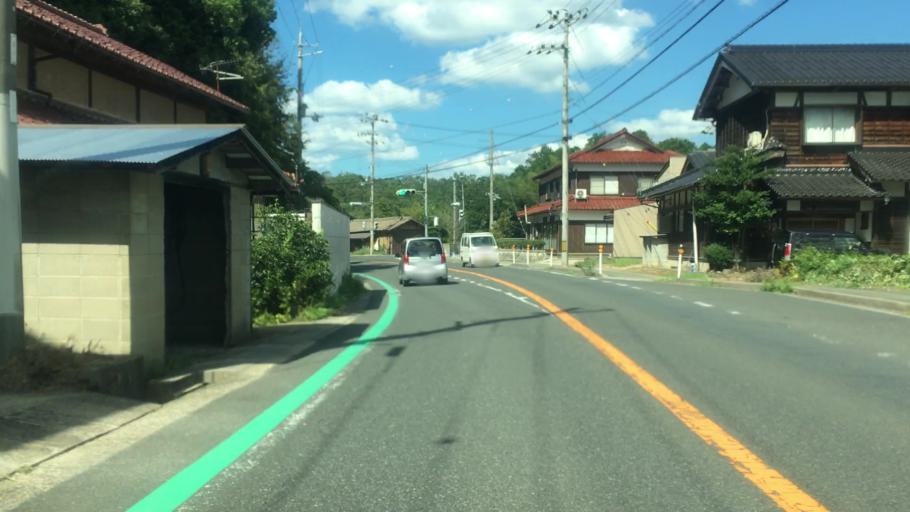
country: JP
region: Kyoto
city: Miyazu
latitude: 35.6122
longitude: 135.0541
